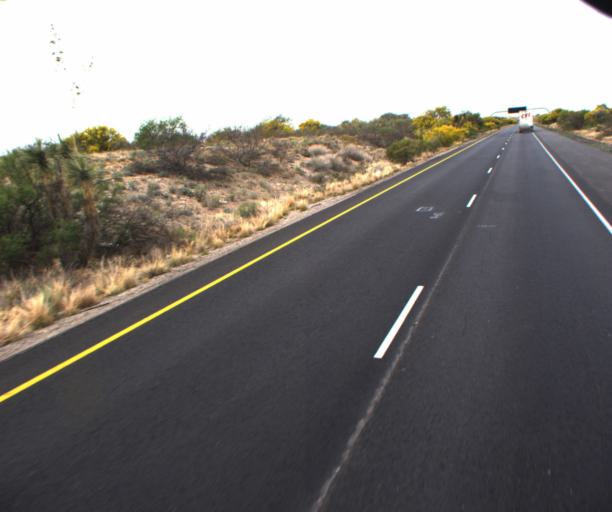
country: US
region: Arizona
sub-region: Pima County
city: Vail
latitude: 32.0007
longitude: -110.6748
